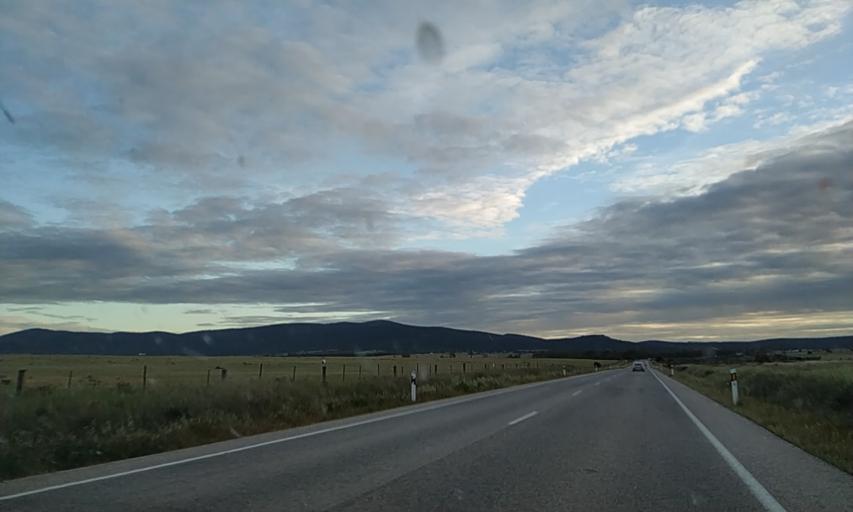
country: ES
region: Extremadura
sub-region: Provincia de Caceres
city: Malpartida de Caceres
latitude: 39.3405
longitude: -6.4778
